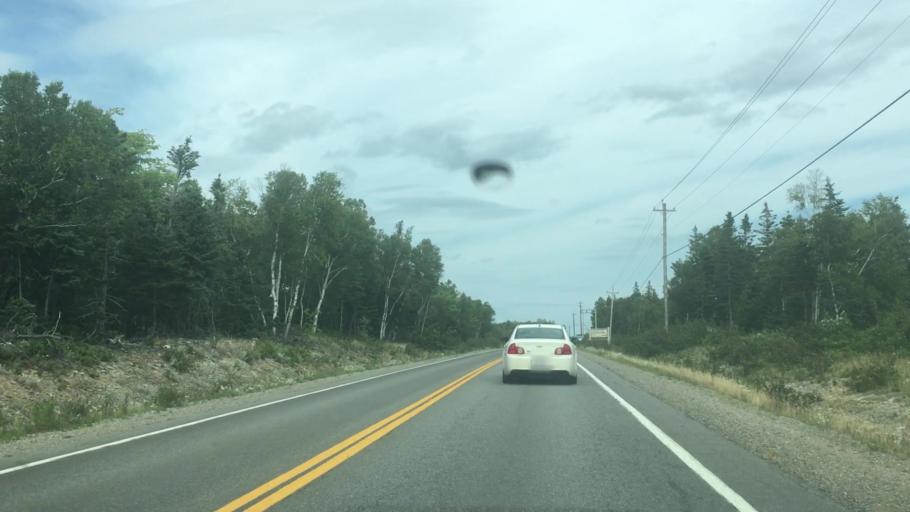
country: CA
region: Nova Scotia
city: Sydney Mines
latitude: 46.5190
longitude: -60.4239
